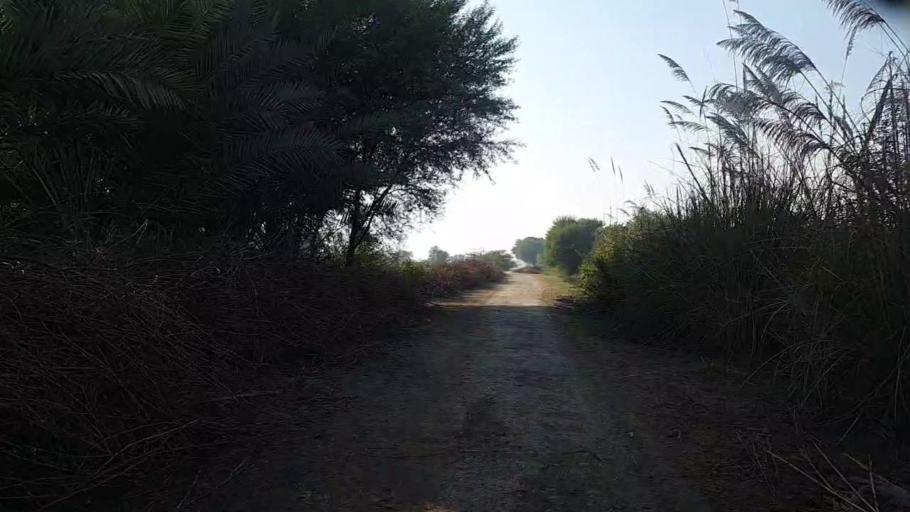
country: PK
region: Sindh
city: Ranipur
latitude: 27.2522
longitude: 68.5471
